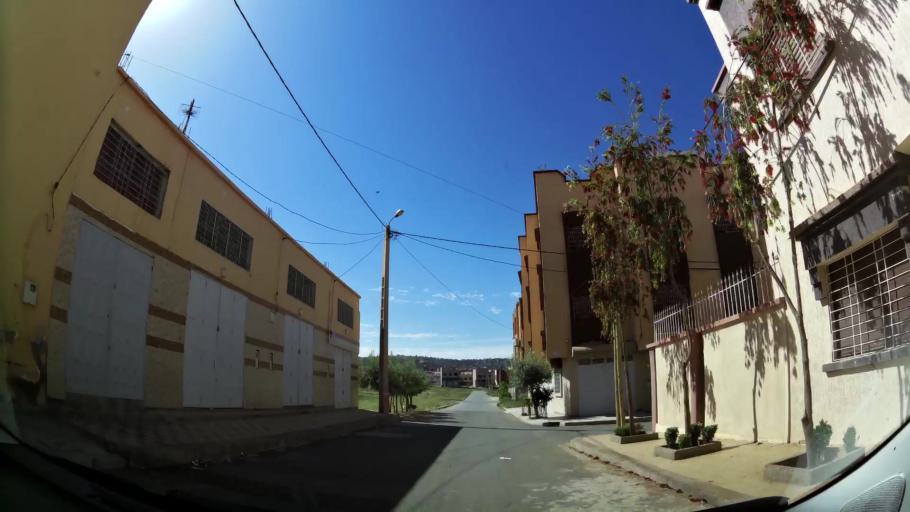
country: MA
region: Oriental
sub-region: Oujda-Angad
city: Oujda
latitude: 34.6547
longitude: -1.8876
